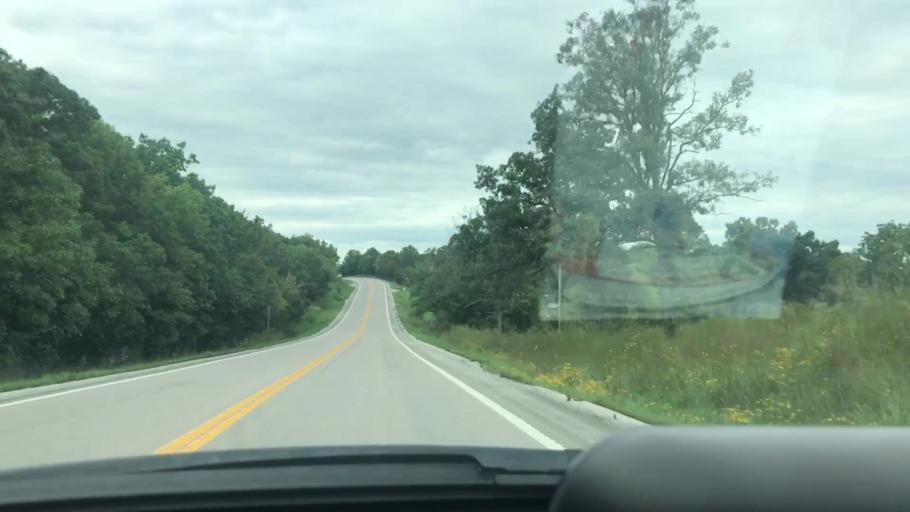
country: US
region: Missouri
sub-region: Benton County
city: Warsaw
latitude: 38.1666
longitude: -93.3086
